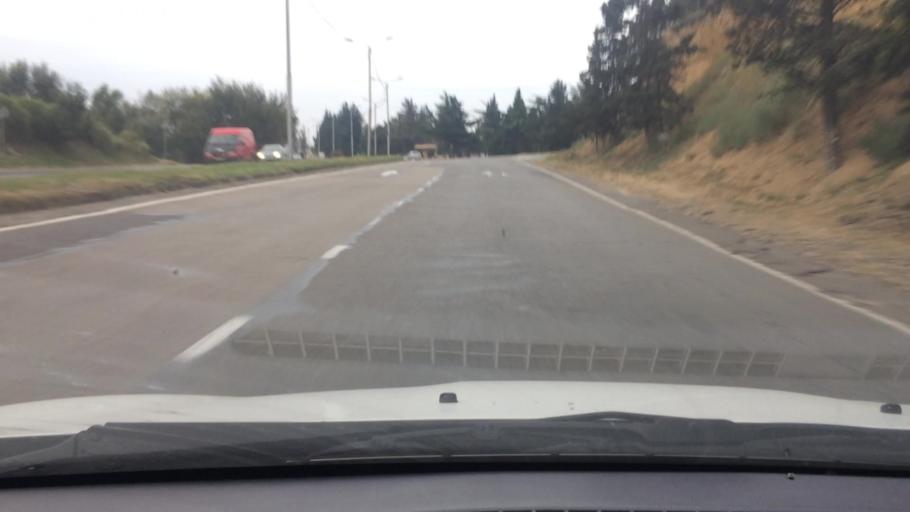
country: GE
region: T'bilisi
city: Tbilisi
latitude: 41.6496
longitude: 44.9041
